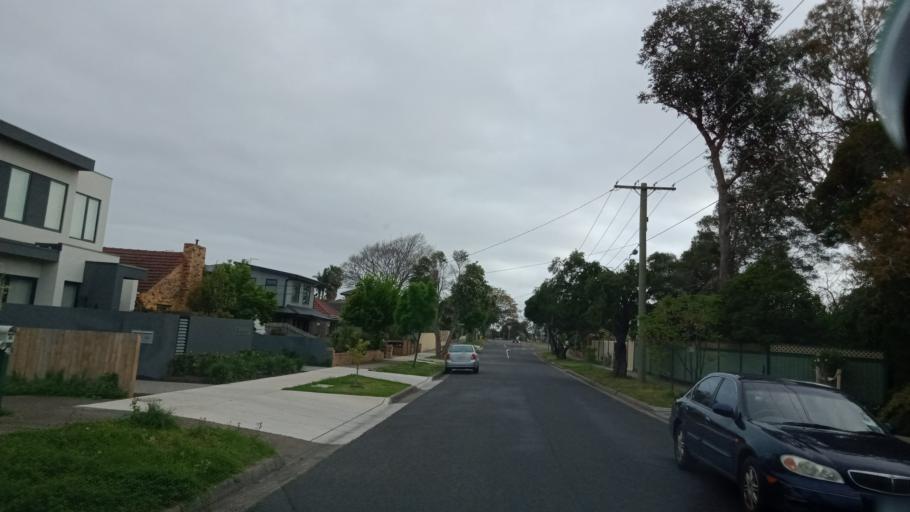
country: AU
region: Victoria
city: McKinnon
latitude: -37.9235
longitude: 145.0617
